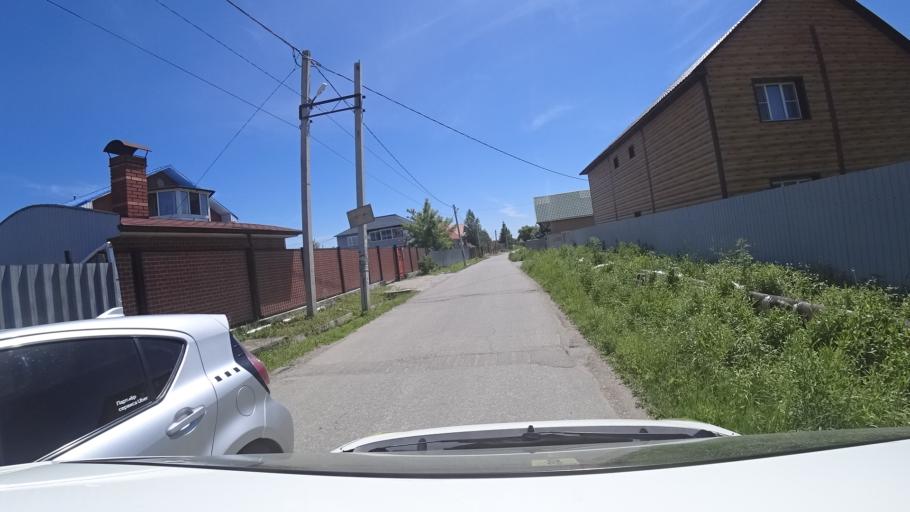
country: RU
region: Khabarovsk Krai
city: Topolevo
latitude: 48.5044
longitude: 135.1754
